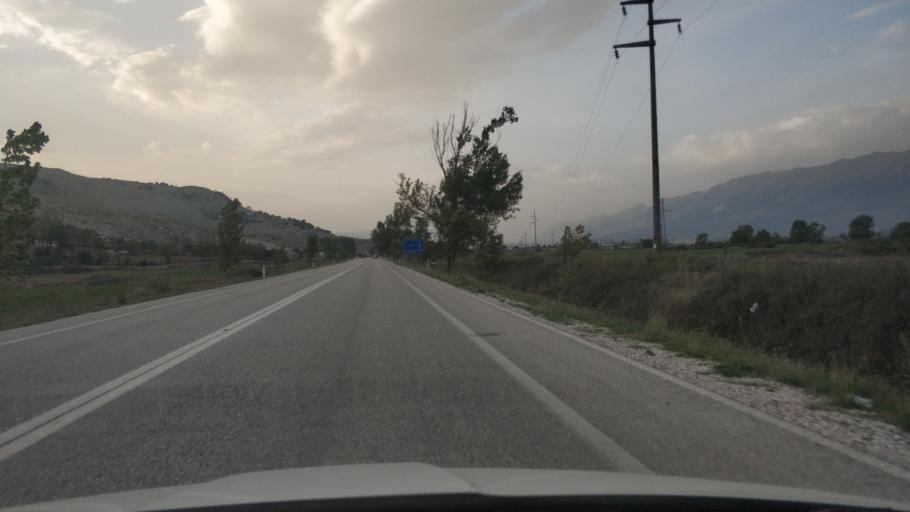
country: AL
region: Gjirokaster
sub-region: Rrethi i Gjirokastres
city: Libohove
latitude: 39.9635
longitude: 20.2428
